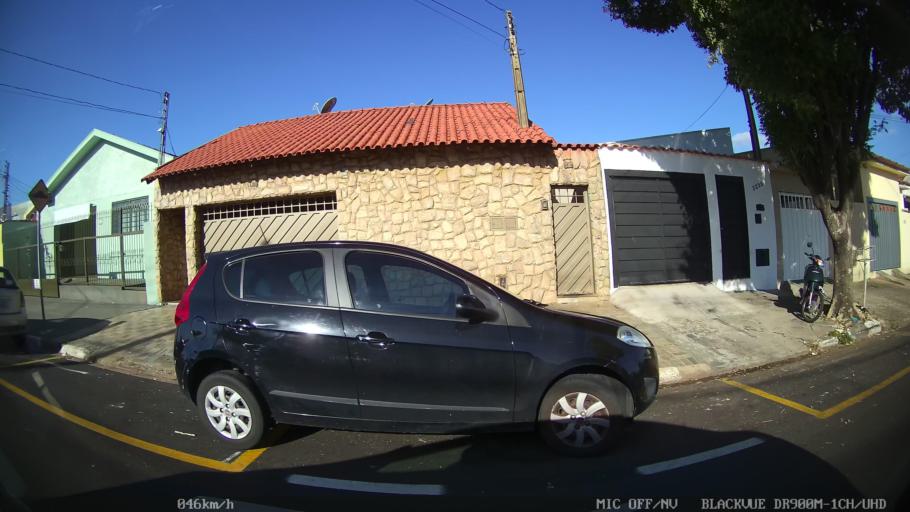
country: BR
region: Sao Paulo
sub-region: Franca
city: Franca
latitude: -20.5203
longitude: -47.4147
